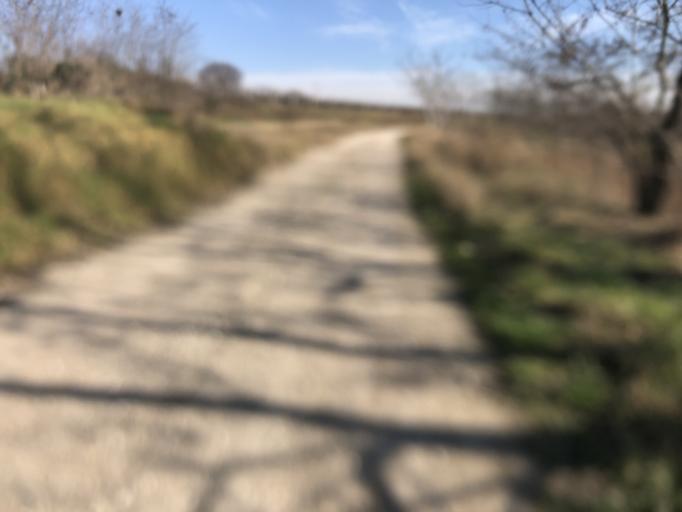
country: IT
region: Veneto
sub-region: Provincia di Verona
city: Valeggio sul Mincio
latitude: 45.3807
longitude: 10.7551
